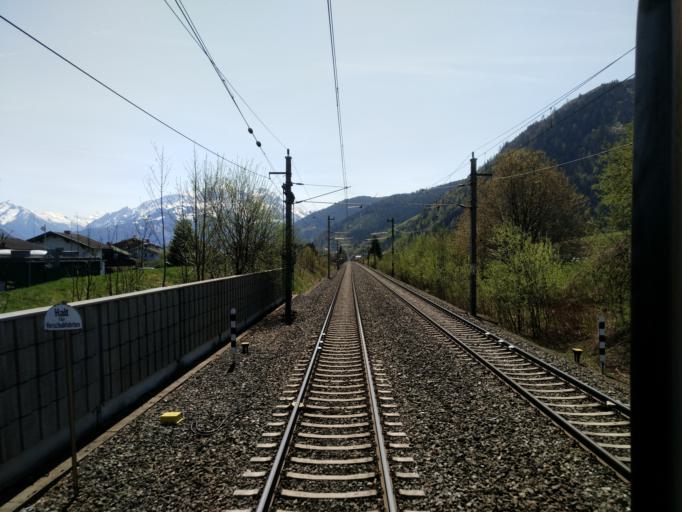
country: AT
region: Salzburg
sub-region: Politischer Bezirk Zell am See
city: Maishofen
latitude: 47.3548
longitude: 12.8078
